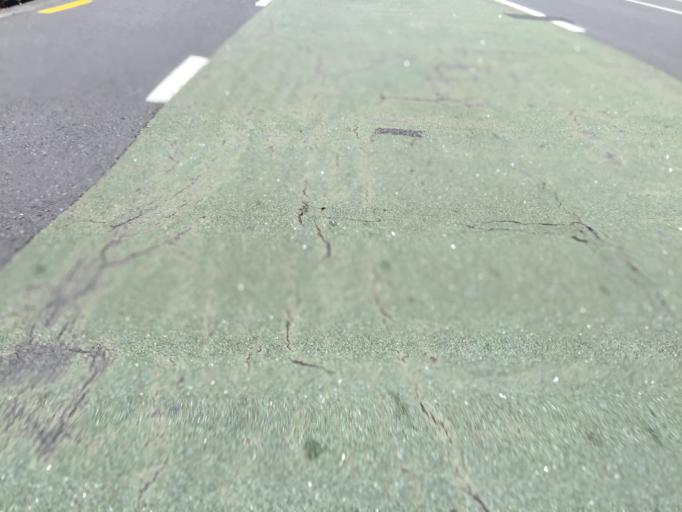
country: NZ
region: Auckland
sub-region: Auckland
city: Auckland
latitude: -36.8548
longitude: 174.7675
